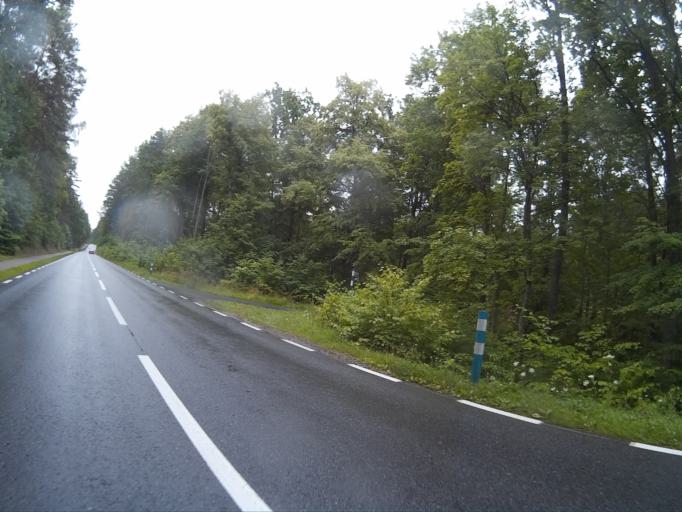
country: PL
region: Kujawsko-Pomorskie
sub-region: Powiat swiecki
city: Osie
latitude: 53.6095
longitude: 18.3038
